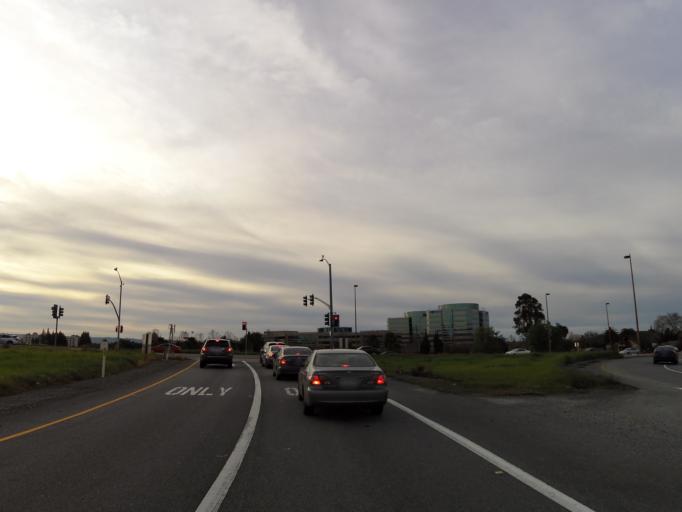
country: US
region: California
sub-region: Santa Clara County
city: Santa Clara
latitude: 37.3867
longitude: -121.9757
